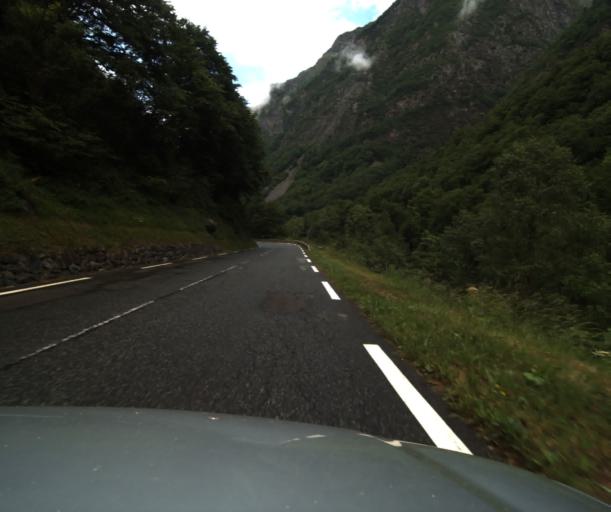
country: FR
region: Midi-Pyrenees
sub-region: Departement des Hautes-Pyrenees
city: Luz-Saint-Sauveur
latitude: 42.8261
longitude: 0.0084
